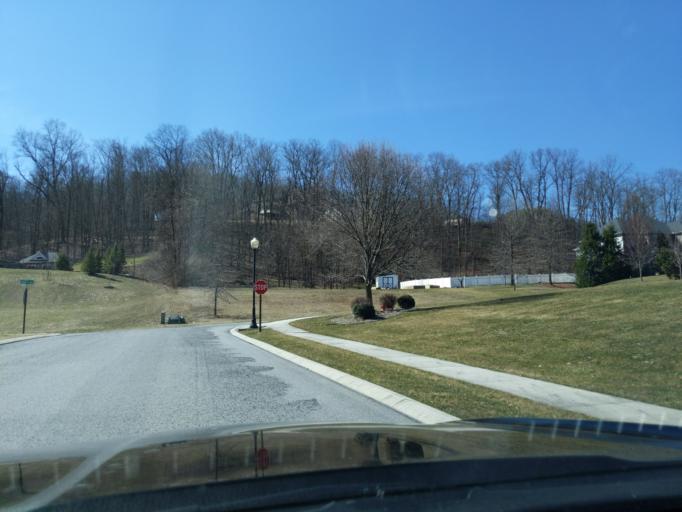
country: US
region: Pennsylvania
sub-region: Blair County
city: Duncansville
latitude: 40.4104
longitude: -78.4210
